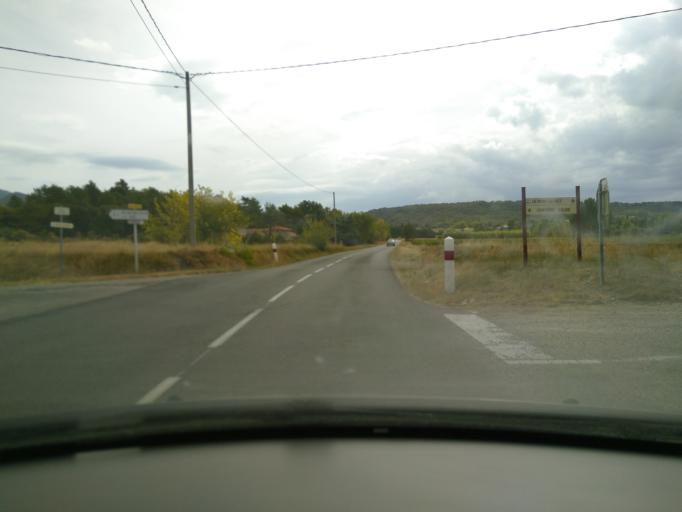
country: FR
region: Rhone-Alpes
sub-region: Departement de la Drome
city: Taulignan
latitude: 44.4343
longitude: 5.0223
